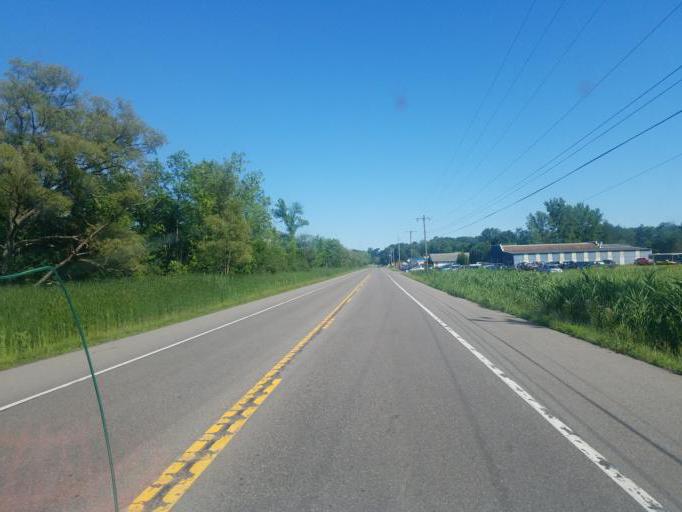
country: US
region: New York
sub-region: Wayne County
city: Lyons
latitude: 43.0644
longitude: -77.0250
